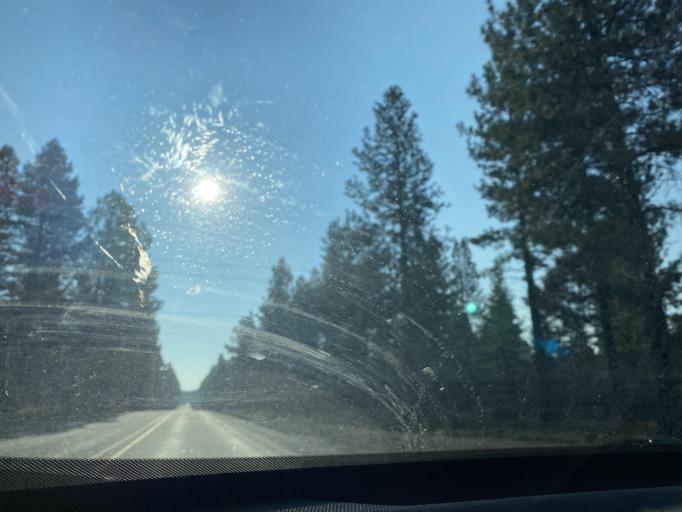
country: US
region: Oregon
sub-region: Deschutes County
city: Sunriver
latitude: 43.8694
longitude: -121.4265
